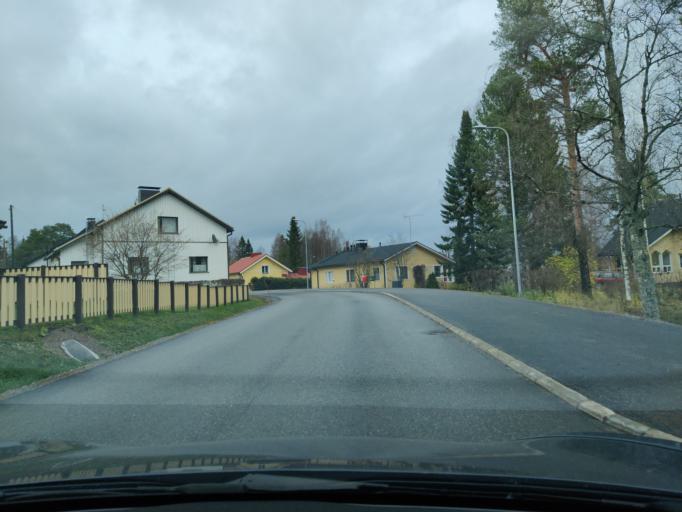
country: FI
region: Northern Savo
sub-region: Ylae-Savo
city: Kiuruvesi
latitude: 63.6490
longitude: 26.6356
